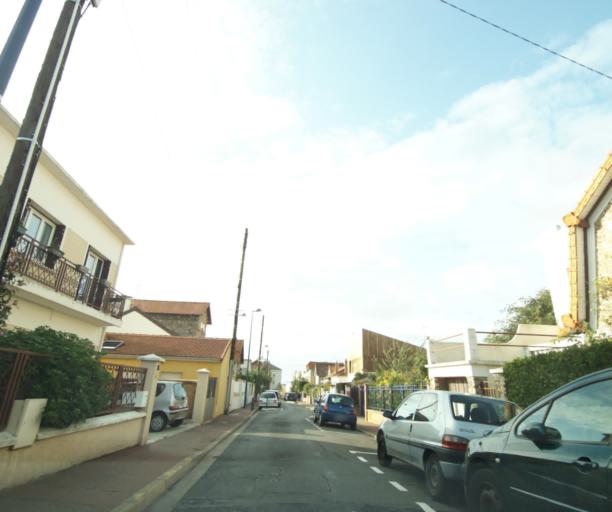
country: FR
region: Ile-de-France
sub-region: Departement des Hauts-de-Seine
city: Clamart
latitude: 48.7993
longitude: 2.2706
